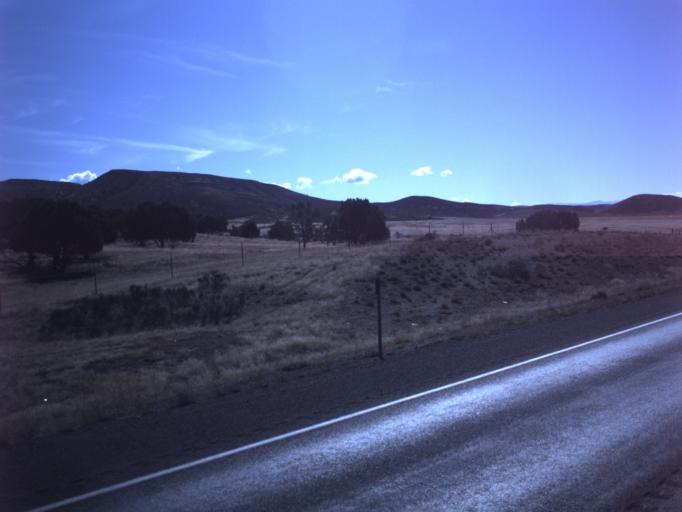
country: US
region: Utah
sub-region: Sanpete County
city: Gunnison
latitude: 39.2204
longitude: -111.8482
